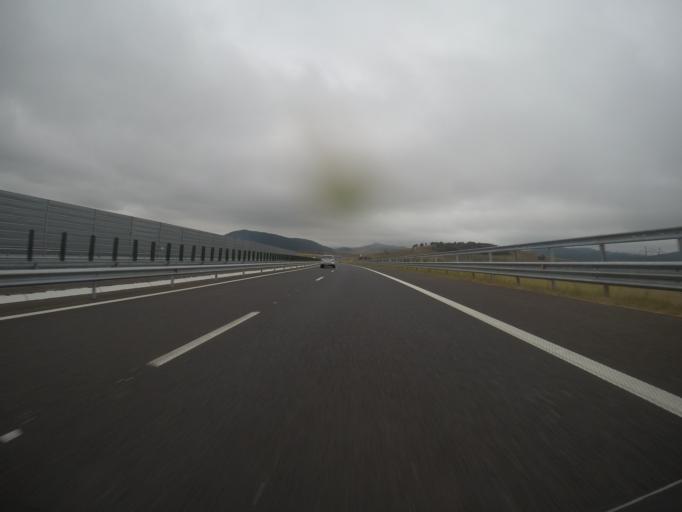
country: RO
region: Hunedoara
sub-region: Comuna Branisca
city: Branisca
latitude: 45.9241
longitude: 22.7767
